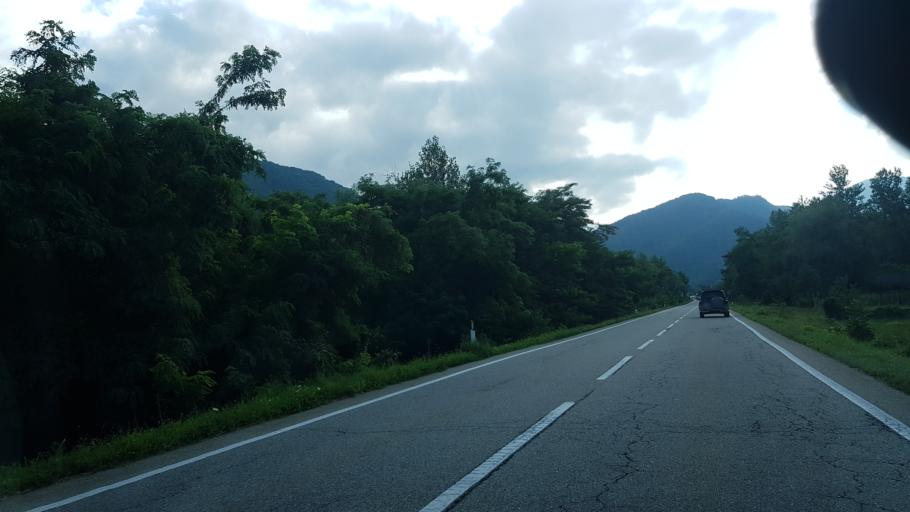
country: IT
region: Piedmont
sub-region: Provincia di Cuneo
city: Brossasco
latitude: 44.5682
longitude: 7.3796
